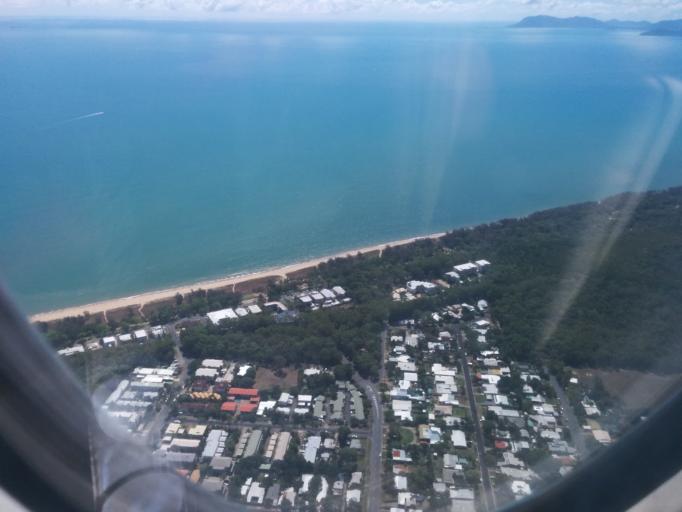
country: AU
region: Queensland
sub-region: Cairns
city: Yorkeys Knob
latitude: -16.8101
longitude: 145.7185
